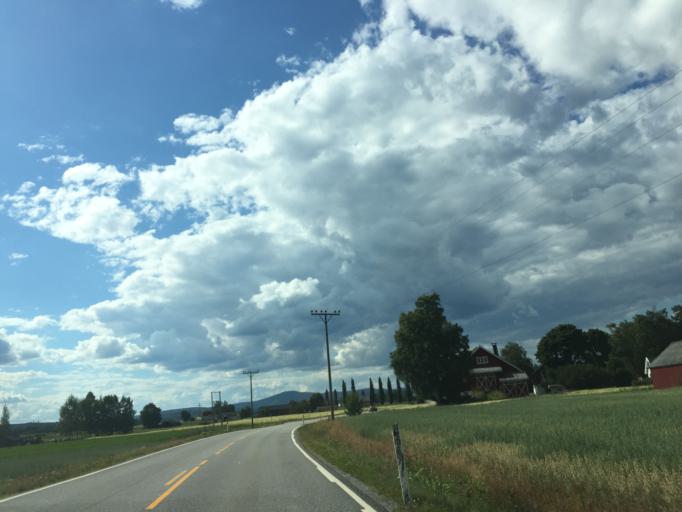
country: NO
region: Hedmark
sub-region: Sor-Odal
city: Skarnes
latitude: 60.2334
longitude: 11.7835
